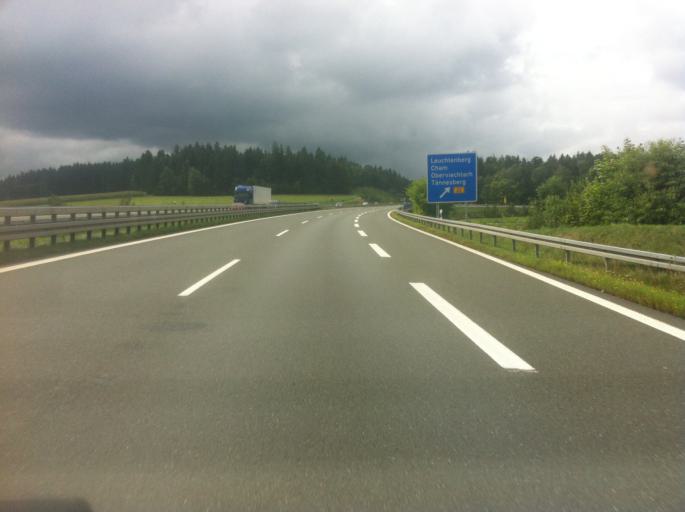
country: DE
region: Bavaria
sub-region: Upper Palatinate
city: Leuchtenberg
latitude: 49.5778
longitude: 12.2749
